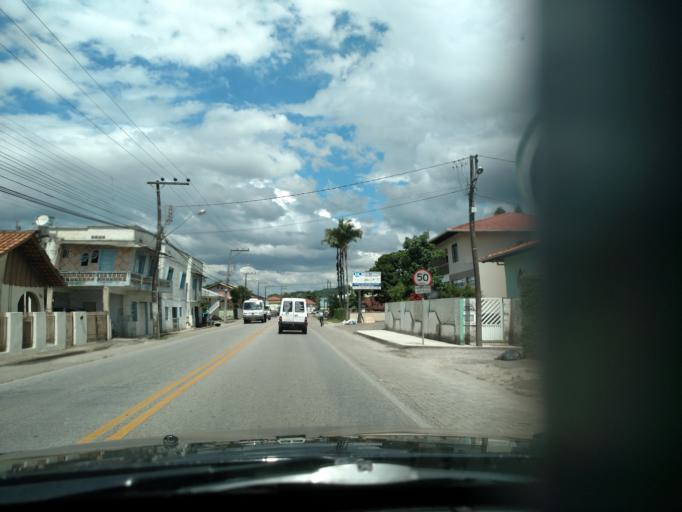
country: BR
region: Santa Catarina
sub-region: Gaspar
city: Gaspar
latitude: -26.9219
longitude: -48.9703
